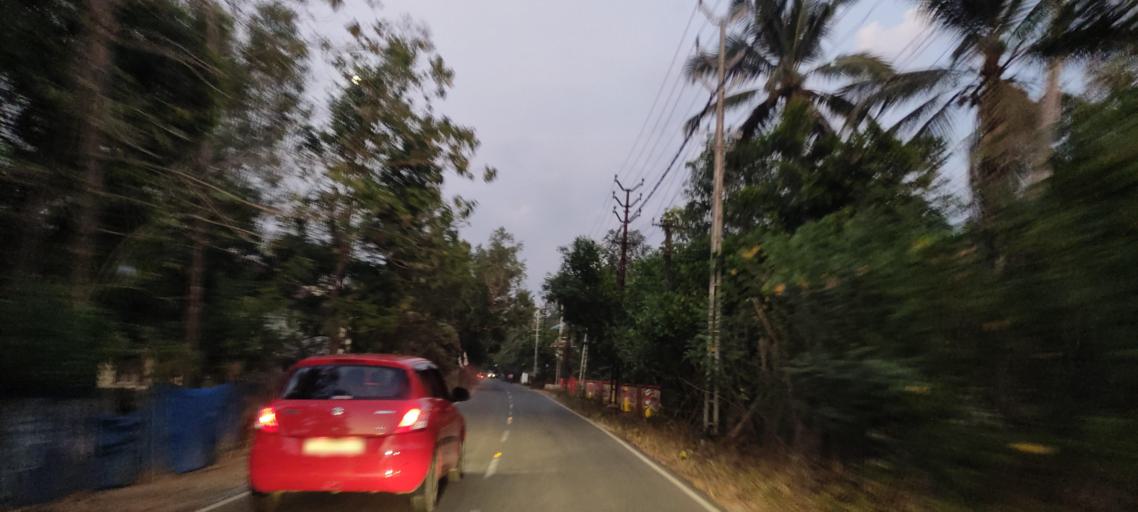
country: IN
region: Kerala
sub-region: Alappuzha
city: Kutiatodu
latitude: 9.7740
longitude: 76.3579
